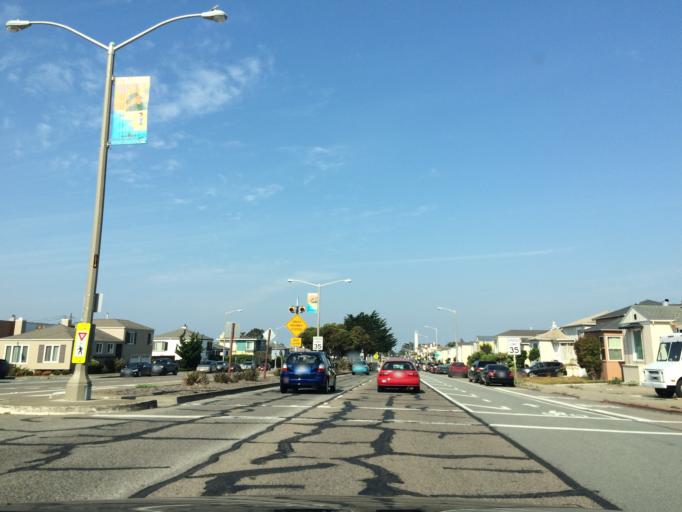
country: US
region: California
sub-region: San Mateo County
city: Daly City
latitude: 37.7343
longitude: -122.4858
